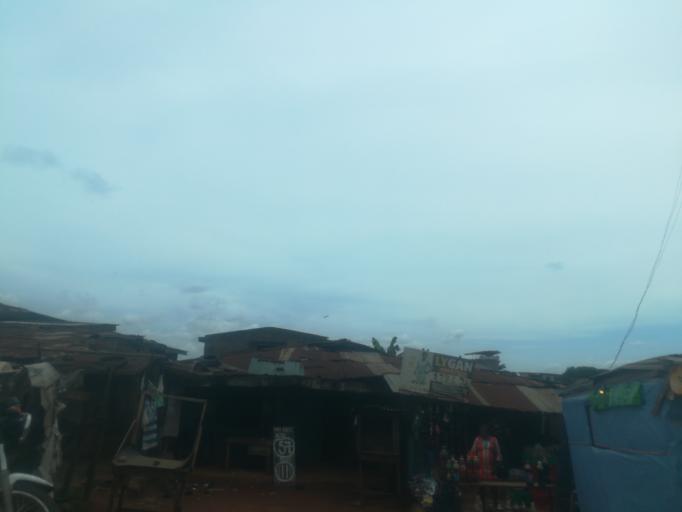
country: NG
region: Oyo
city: Ibadan
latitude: 7.3783
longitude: 3.9453
